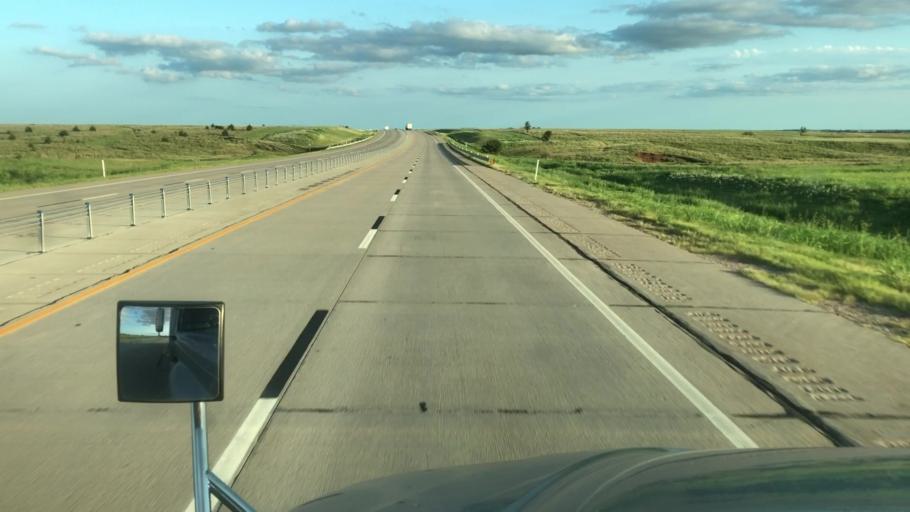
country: US
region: Oklahoma
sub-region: Pawnee County
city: Pawnee
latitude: 36.3528
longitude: -97.0303
